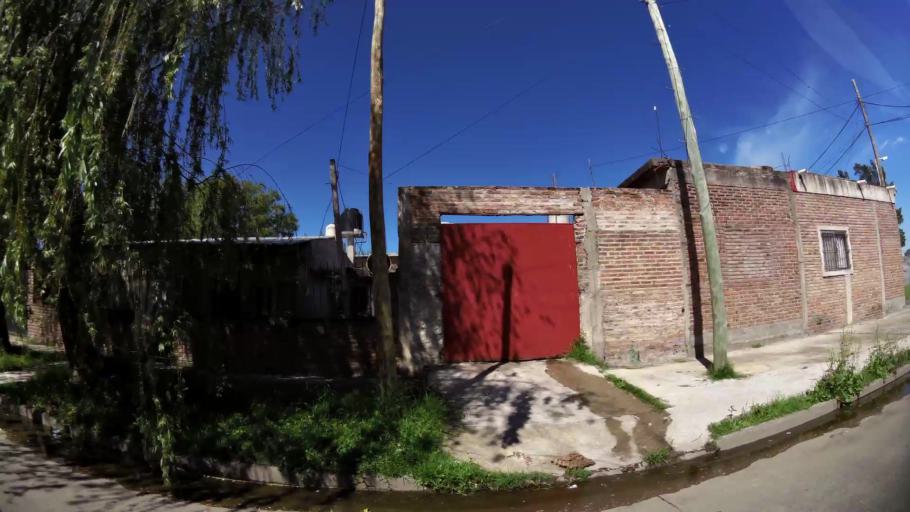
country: AR
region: Buenos Aires
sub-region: Partido de Avellaneda
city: Avellaneda
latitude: -34.6858
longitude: -58.3094
